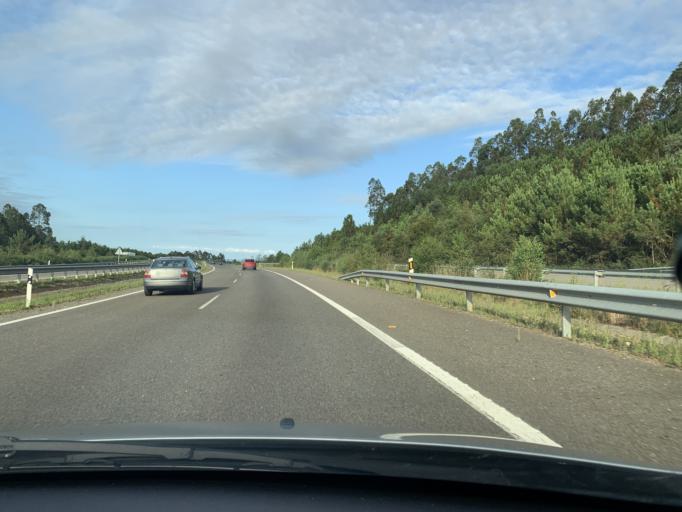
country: ES
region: Galicia
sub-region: Provincia de Lugo
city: Barreiros
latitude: 43.5352
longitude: -7.2287
